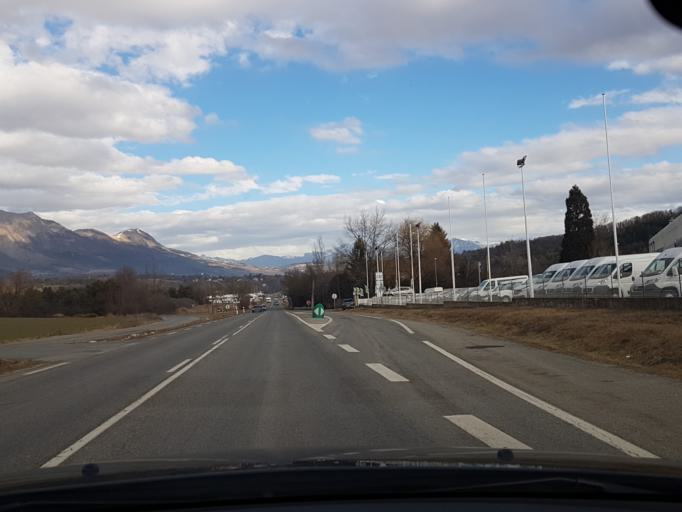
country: FR
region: Provence-Alpes-Cote d'Azur
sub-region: Departement des Hautes-Alpes
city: Tallard
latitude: 44.5026
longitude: 6.0435
